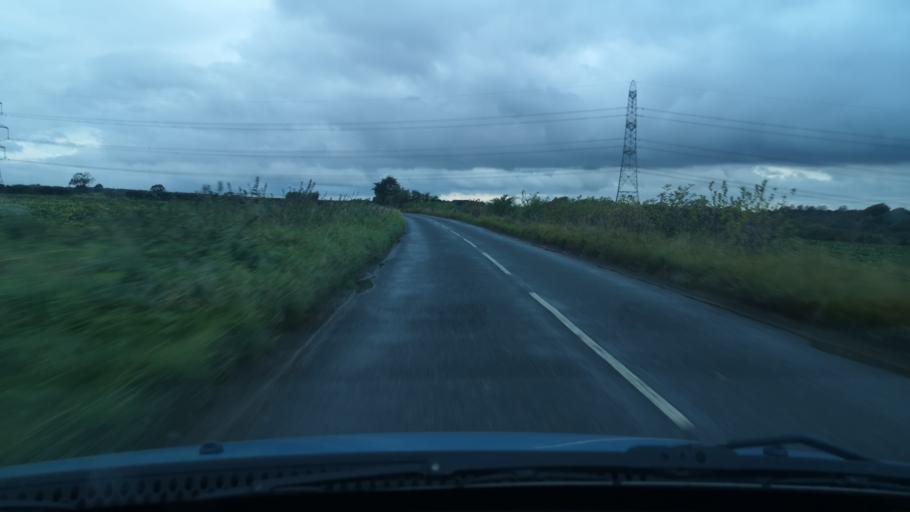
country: GB
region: England
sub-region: City and Borough of Wakefield
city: Darrington
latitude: 53.6455
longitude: -1.2308
